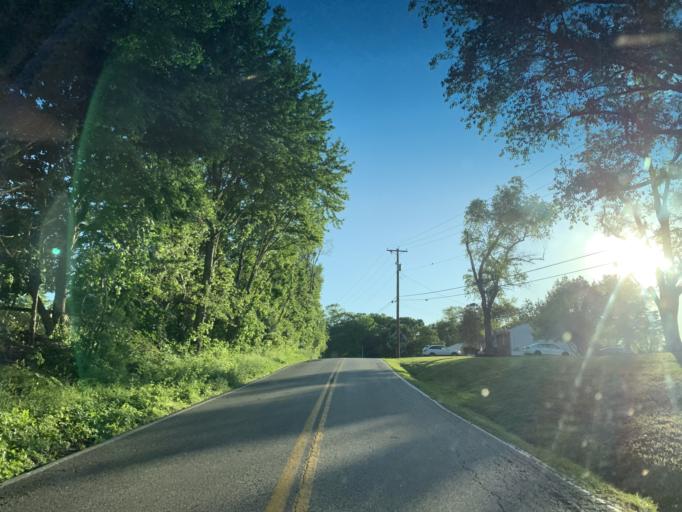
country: US
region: Maryland
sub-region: Cecil County
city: Elkton
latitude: 39.6657
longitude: -75.8420
